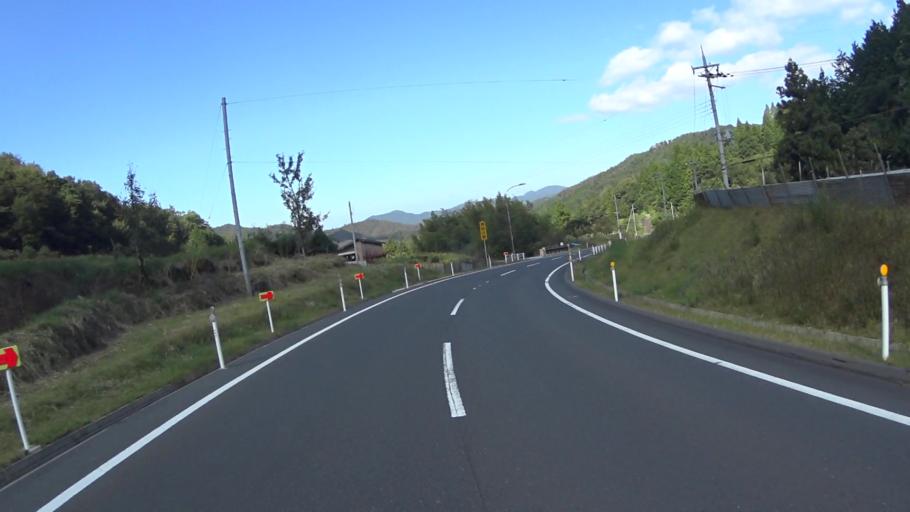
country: JP
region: Hyogo
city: Toyooka
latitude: 35.5400
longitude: 134.9785
